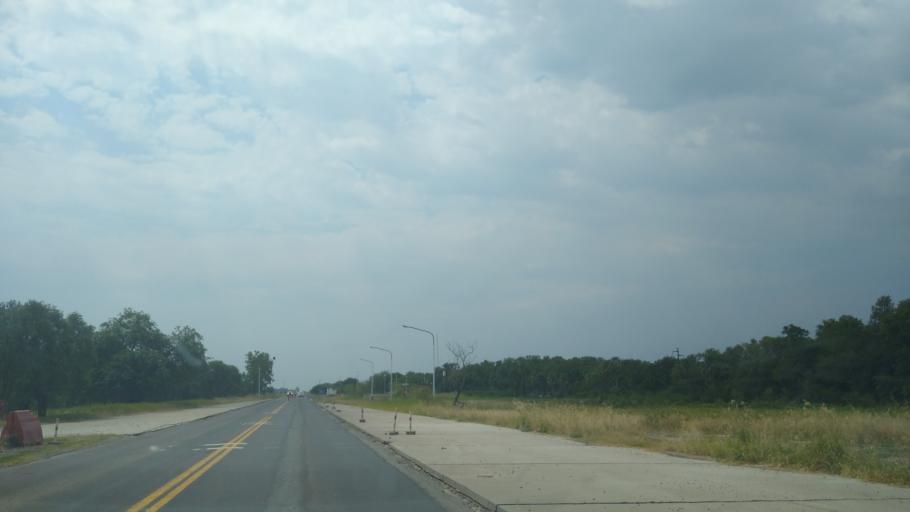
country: AR
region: Chaco
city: Margarita Belen
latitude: -27.1193
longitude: -58.9712
